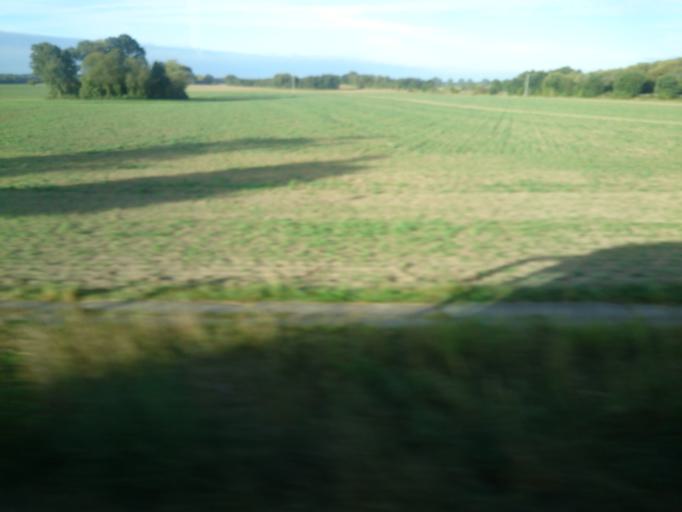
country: DE
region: Mecklenburg-Vorpommern
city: Zussow
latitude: 53.9807
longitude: 13.6100
